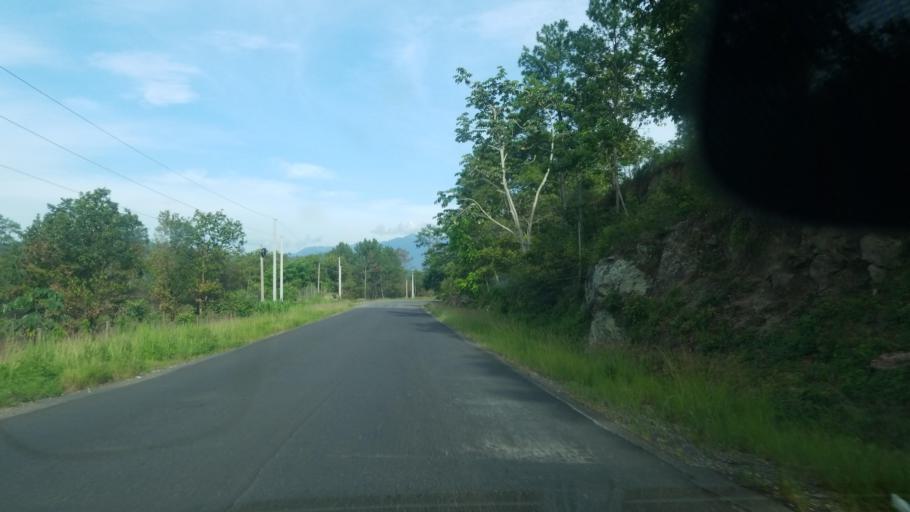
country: HN
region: Santa Barbara
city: Trinidad
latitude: 15.1701
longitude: -88.2608
